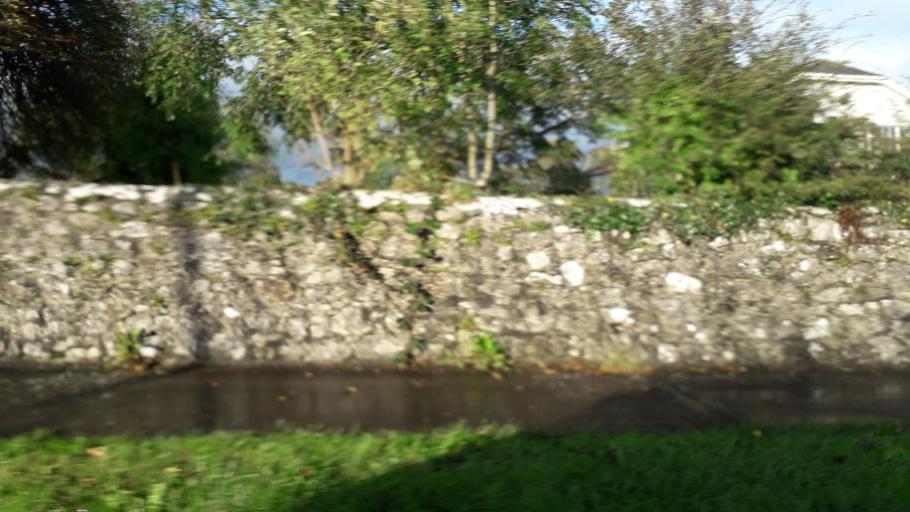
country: IE
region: Connaught
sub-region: Roscommon
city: Castlerea
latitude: 53.8705
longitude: -8.4104
